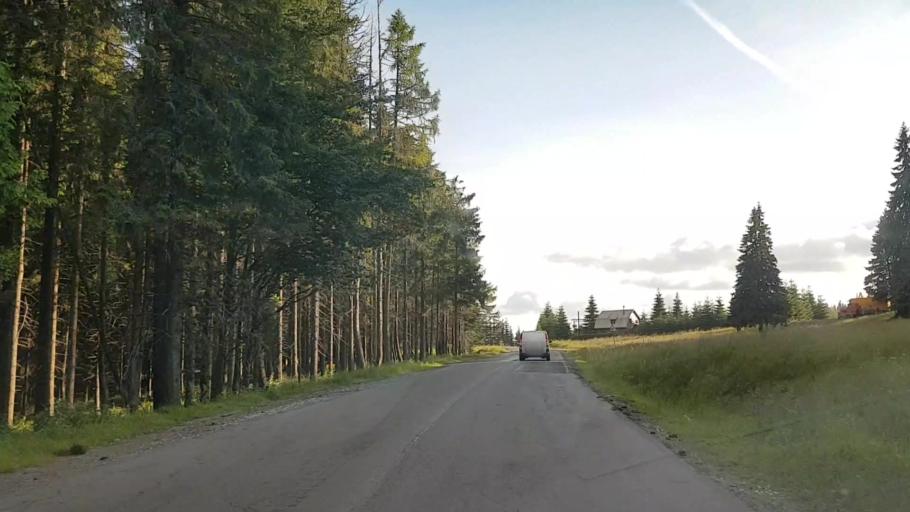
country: RO
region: Harghita
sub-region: Comuna Varsag
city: Varsag
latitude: 46.6570
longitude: 25.2983
